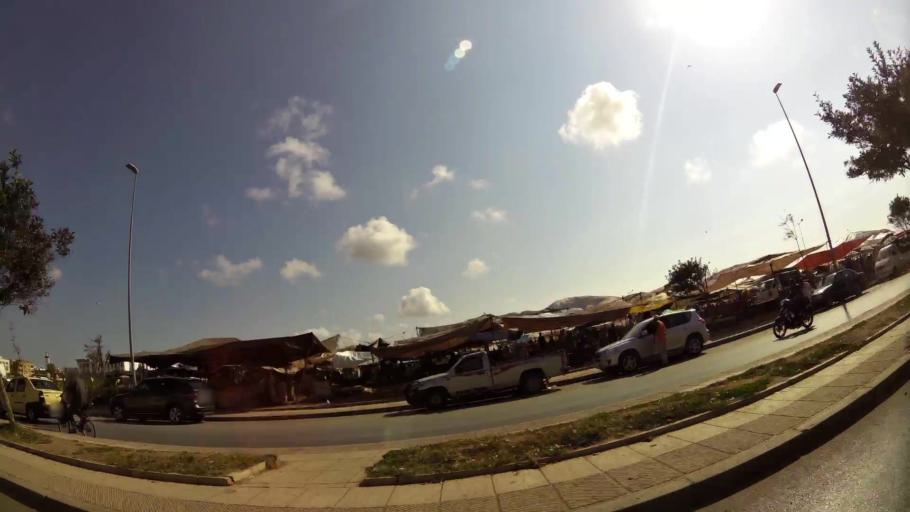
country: MA
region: Rabat-Sale-Zemmour-Zaer
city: Sale
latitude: 34.0501
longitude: -6.7890
